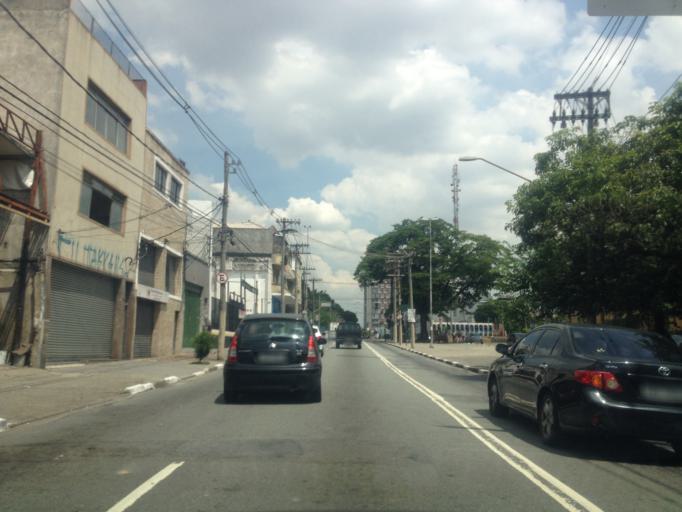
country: BR
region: Sao Paulo
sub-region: Sao Paulo
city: Sao Paulo
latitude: -23.5327
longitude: -46.6315
